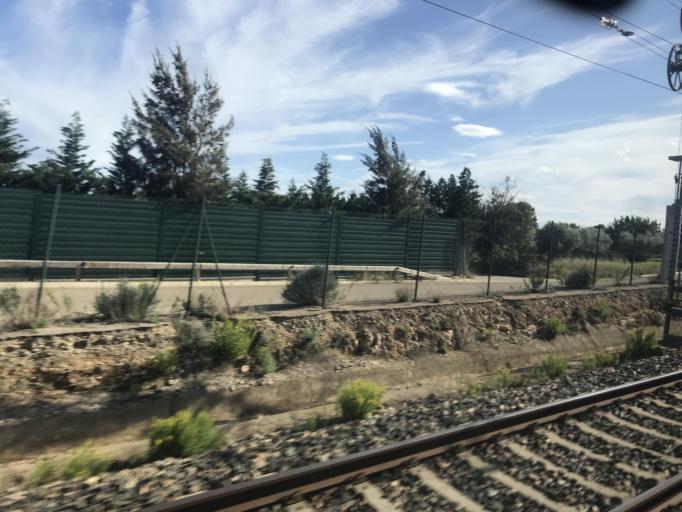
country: ES
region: Catalonia
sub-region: Provincia de Tarragona
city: l'Ametlla de Mar
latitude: 40.8651
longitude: 0.7769
